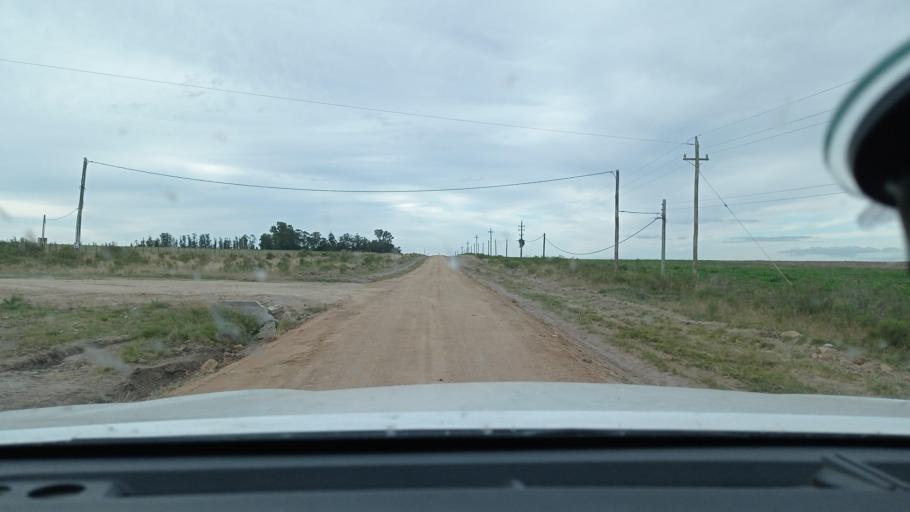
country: UY
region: Florida
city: Casupa
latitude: -34.1154
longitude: -55.7680
